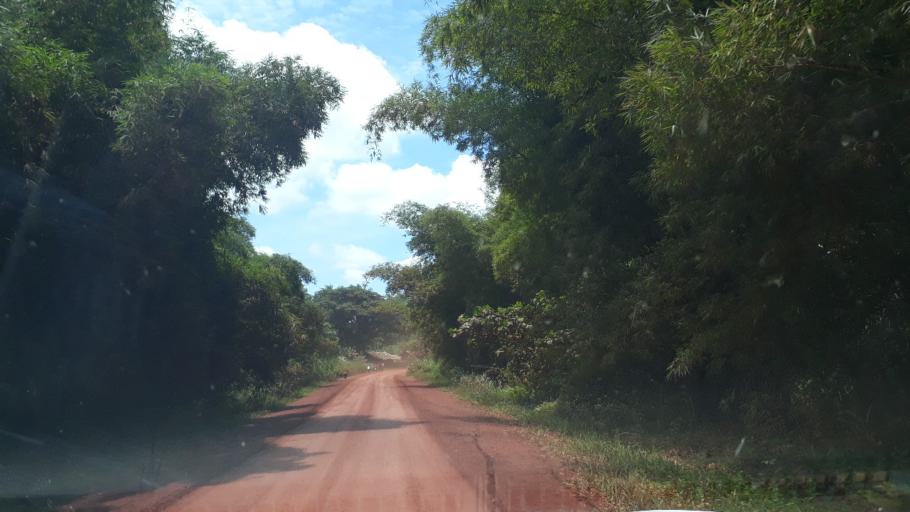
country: CD
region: Eastern Province
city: Kisangani
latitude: 0.5650
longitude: 25.8574
